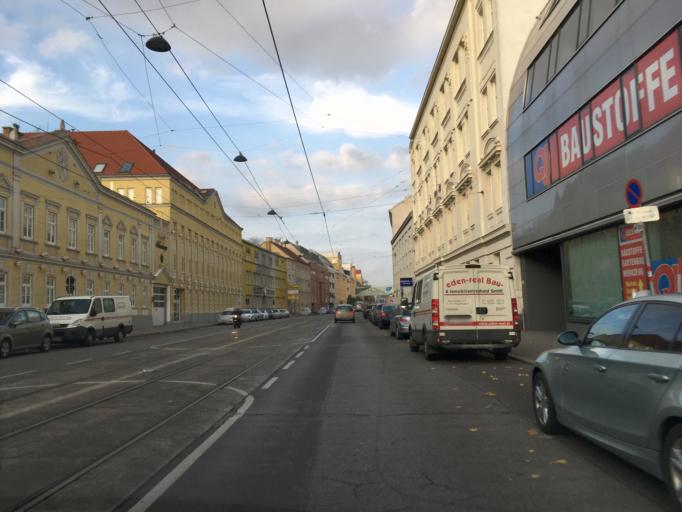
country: AT
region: Vienna
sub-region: Wien Stadt
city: Vienna
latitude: 48.2373
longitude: 16.3577
